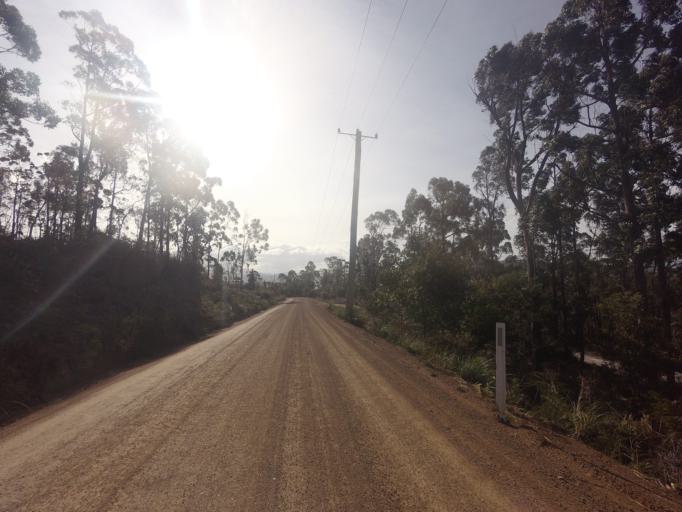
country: AU
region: Tasmania
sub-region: Kingborough
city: Kettering
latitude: -43.0833
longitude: 147.2647
